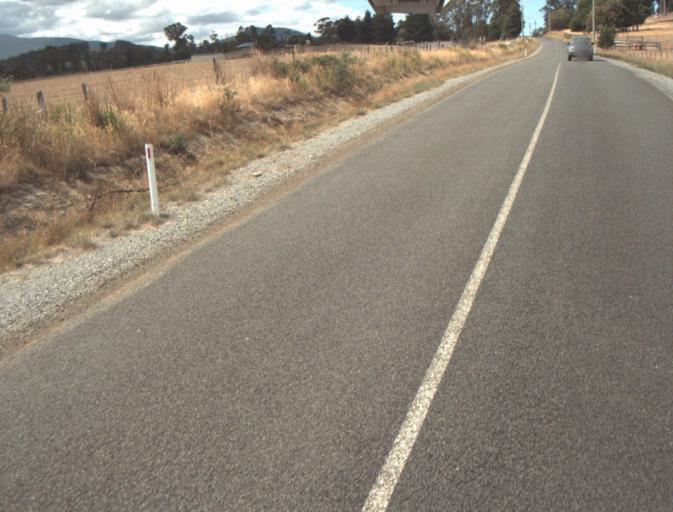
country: AU
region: Tasmania
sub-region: Launceston
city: Mayfield
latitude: -41.2121
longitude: 147.1341
